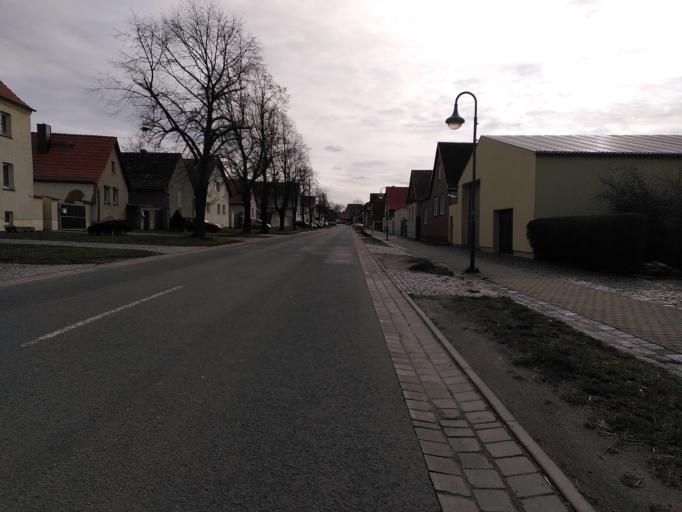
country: DE
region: Saxony-Anhalt
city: Ballenstedt
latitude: 51.7692
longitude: 11.2453
